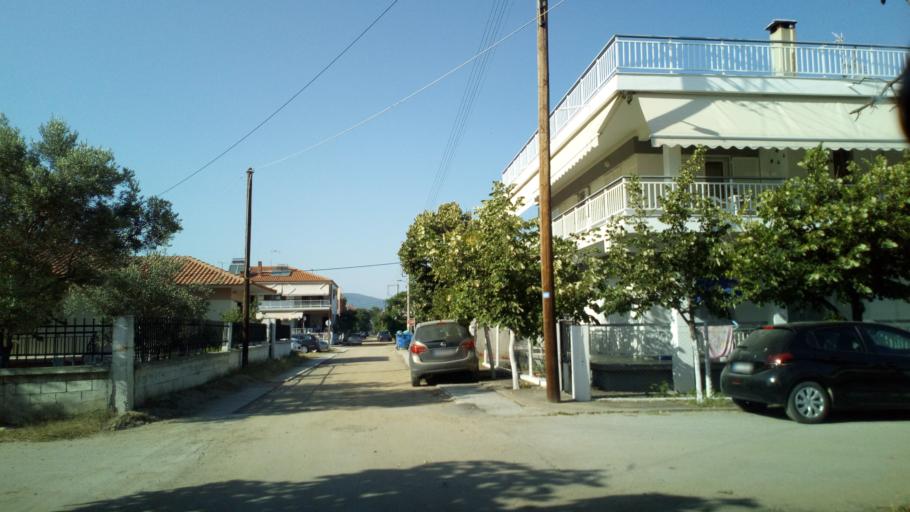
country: GR
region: Central Macedonia
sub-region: Nomos Thessalonikis
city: Nea Vrasna
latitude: 40.7050
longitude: 23.6996
